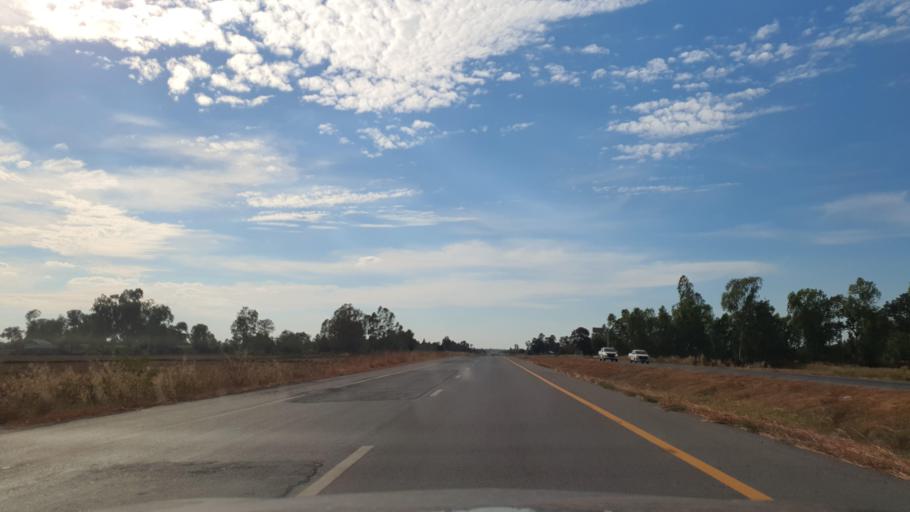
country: TH
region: Roi Et
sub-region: Amphoe Pho Chai
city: Pho Chai
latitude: 16.4134
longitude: 103.7833
